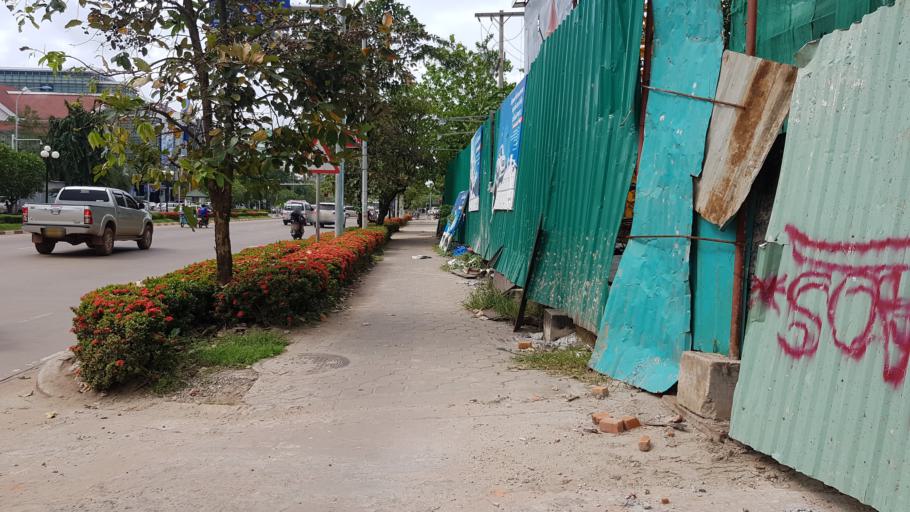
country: LA
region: Vientiane
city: Vientiane
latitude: 17.9689
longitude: 102.6164
